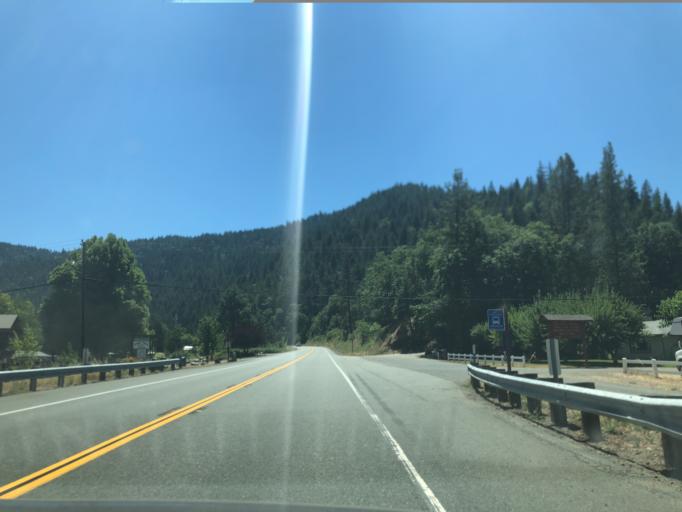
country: US
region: California
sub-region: Trinity County
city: Weaverville
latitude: 40.6569
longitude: -122.9139
